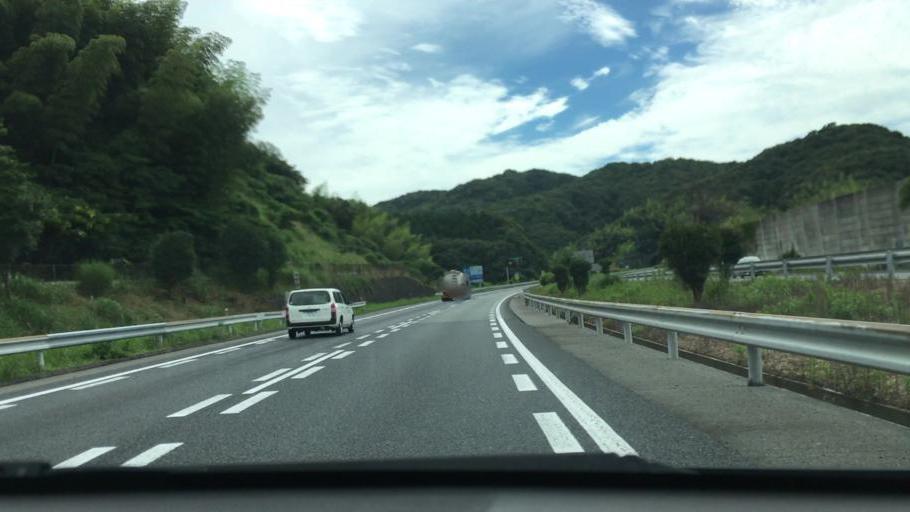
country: JP
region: Yamaguchi
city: Tokuyama
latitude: 34.0663
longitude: 131.7011
